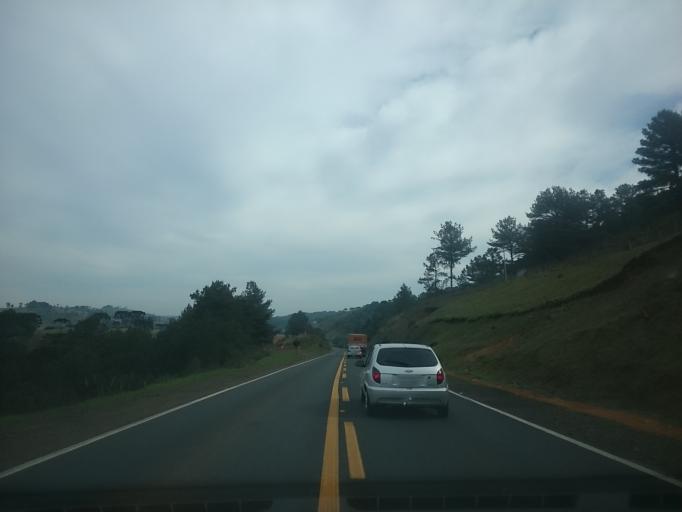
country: BR
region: Santa Catarina
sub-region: Lages
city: Lages
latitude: -27.9797
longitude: -50.5120
